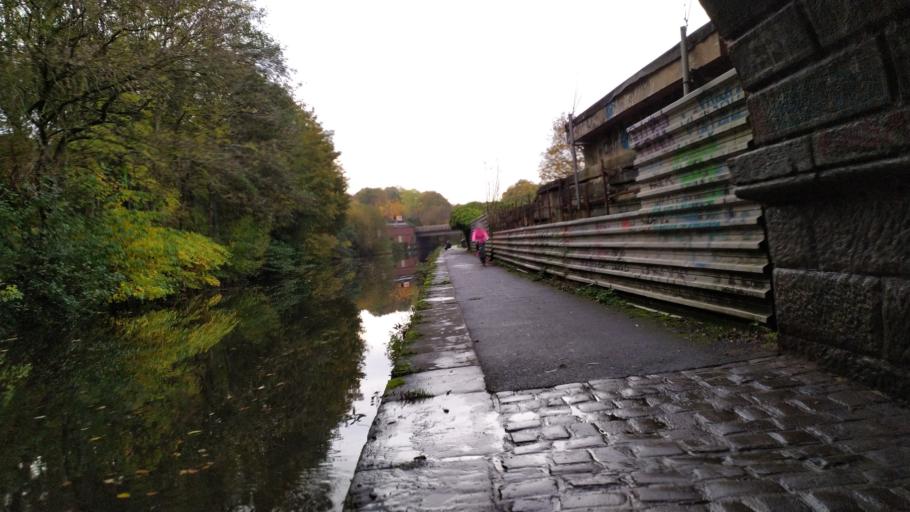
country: GB
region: England
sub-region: City and Borough of Leeds
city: Leeds
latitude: 53.8020
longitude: -1.5777
